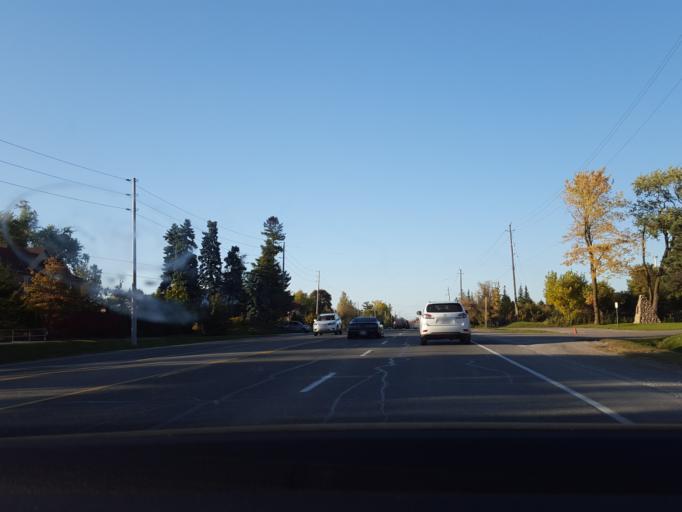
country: CA
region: Ontario
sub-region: York
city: Richmond Hill
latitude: 43.9181
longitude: -79.4482
